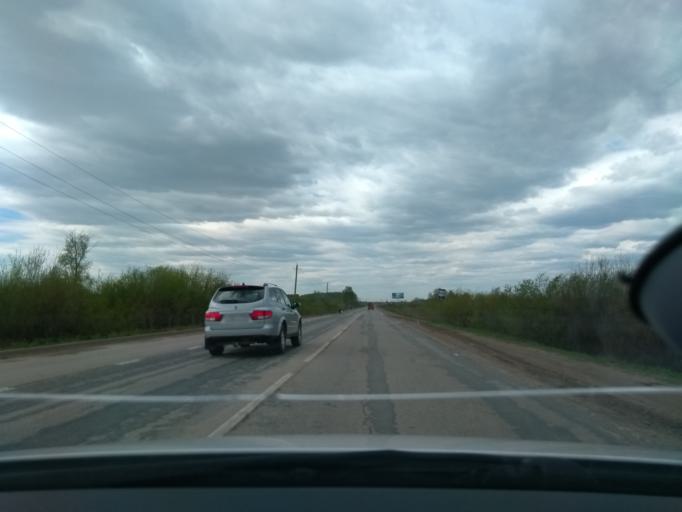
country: RU
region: Perm
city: Lobanovo
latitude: 57.8711
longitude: 56.2830
